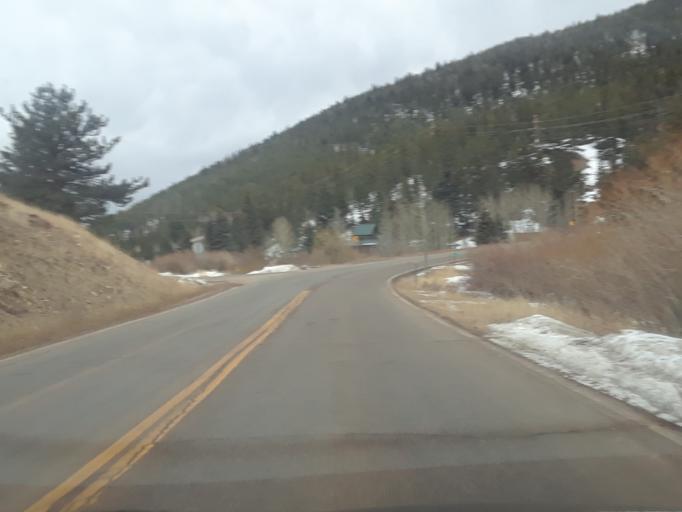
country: US
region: Colorado
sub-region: Boulder County
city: Coal Creek
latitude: 39.8303
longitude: -105.4128
